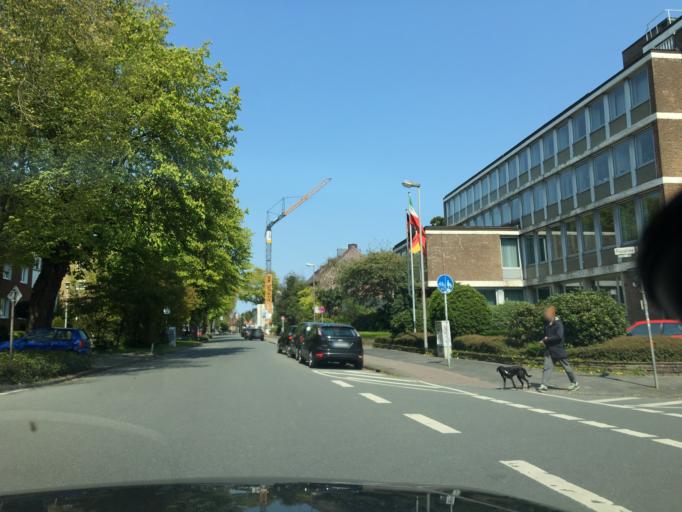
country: DE
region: North Rhine-Westphalia
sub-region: Regierungsbezirk Munster
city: Muenster
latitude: 51.9648
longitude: 7.6382
